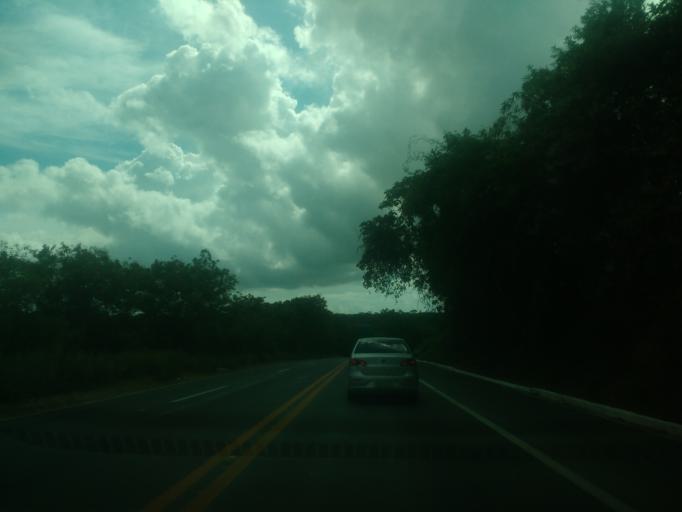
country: BR
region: Alagoas
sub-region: Marechal Deodoro
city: Marechal Deodoro
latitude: -9.6860
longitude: -35.8231
